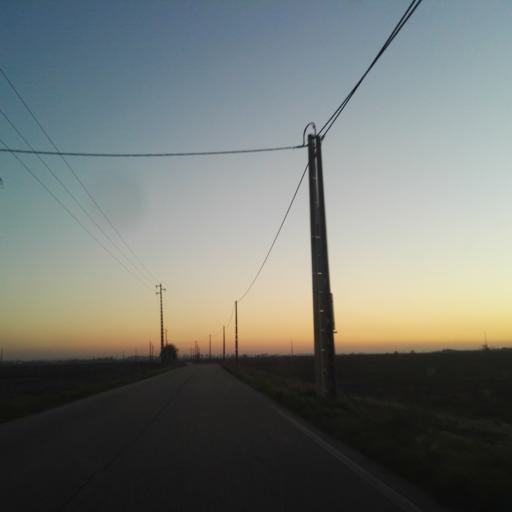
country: PT
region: Santarem
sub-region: Alpiarca
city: Alpiarca
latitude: 39.2814
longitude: -8.5939
